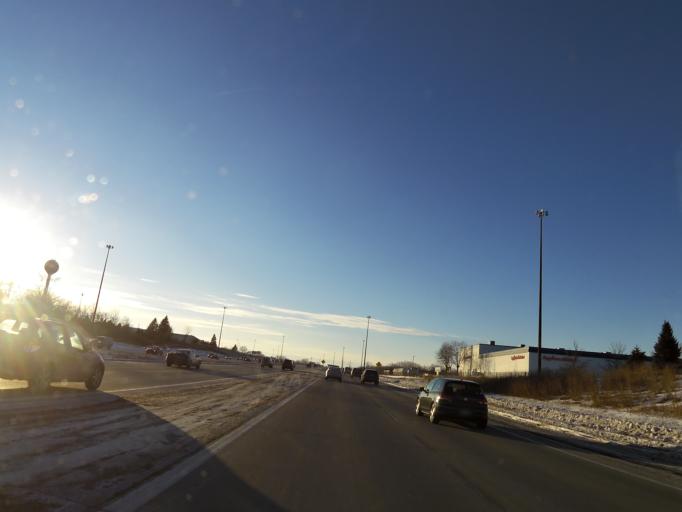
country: US
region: Minnesota
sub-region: Hennepin County
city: Eden Prairie
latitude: 44.8621
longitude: -93.4617
